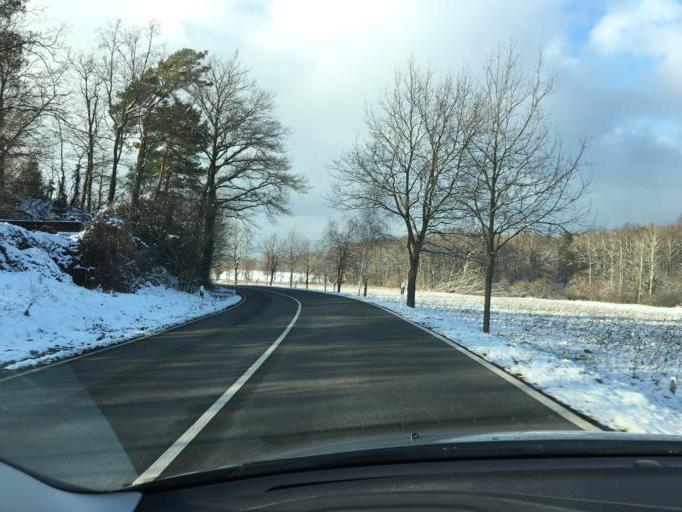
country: DE
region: Saxony
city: Grimma
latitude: 51.2721
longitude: 12.6651
